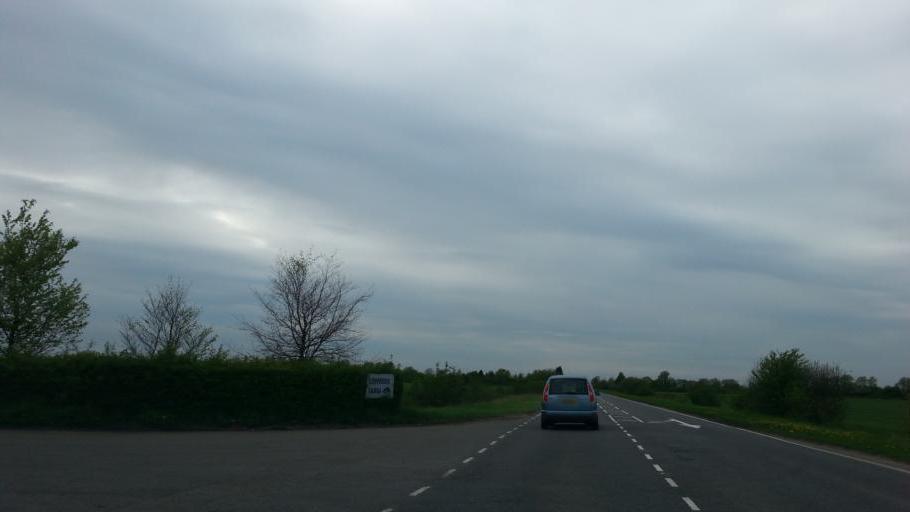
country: GB
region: England
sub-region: Cambridgeshire
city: March
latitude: 52.5246
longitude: 0.0808
